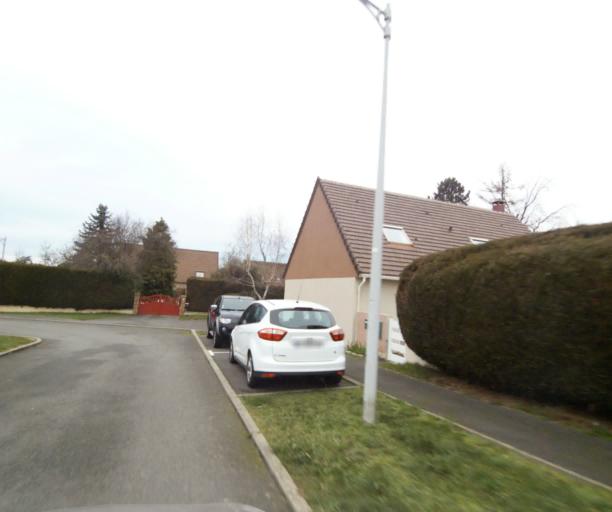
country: FR
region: Ile-de-France
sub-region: Departement de Seine-et-Marne
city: Dammartin-en-Goele
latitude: 49.0590
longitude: 2.6931
